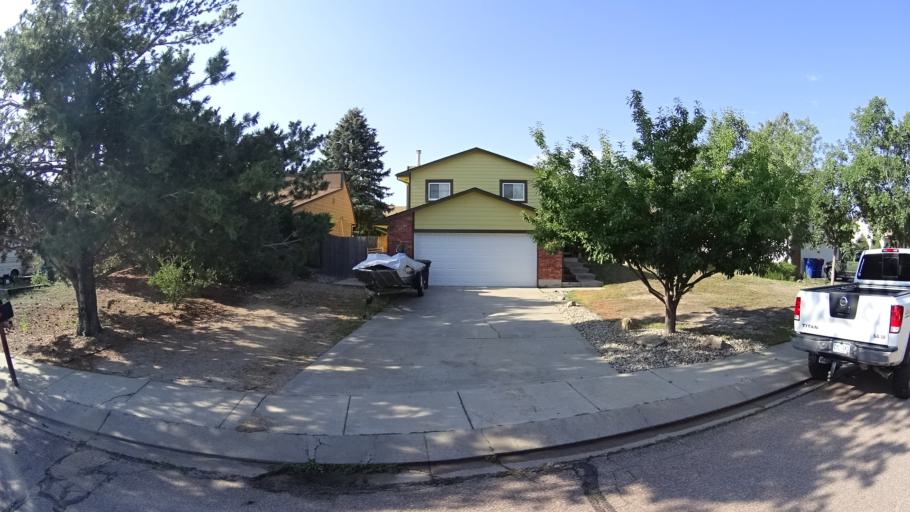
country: US
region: Colorado
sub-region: El Paso County
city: Black Forest
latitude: 38.9432
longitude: -104.7667
